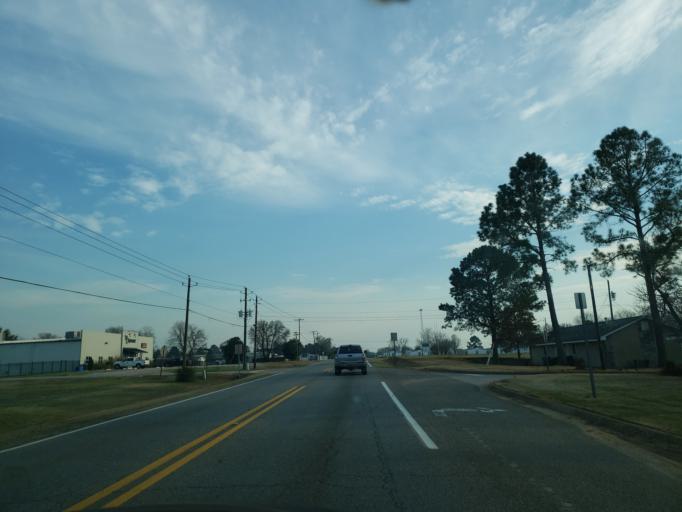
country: US
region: Alabama
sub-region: Hale County
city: Moundville
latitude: 32.9879
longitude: -87.6245
